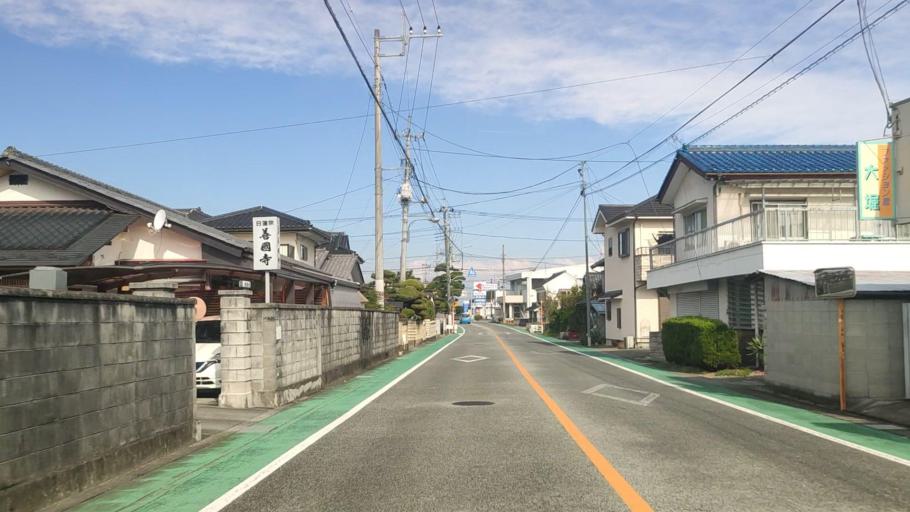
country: JP
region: Yamanashi
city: Ryuo
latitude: 35.5717
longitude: 138.4647
